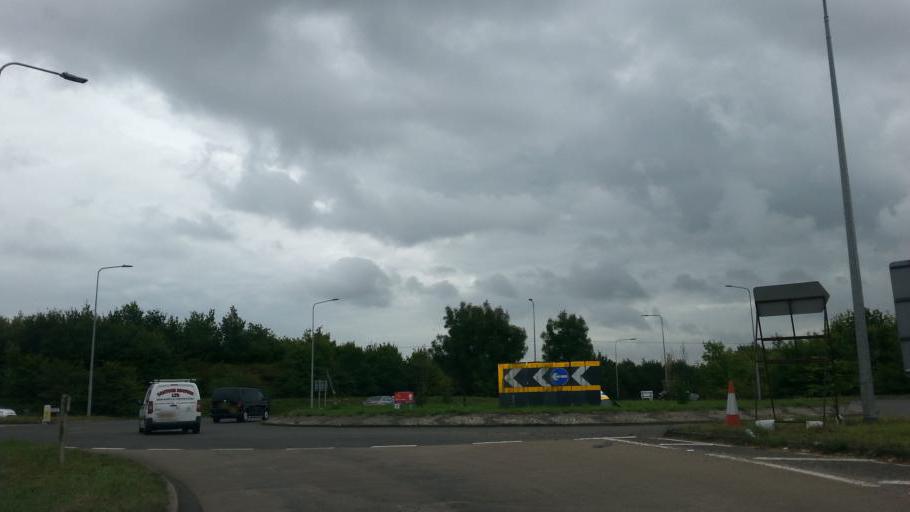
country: GB
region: England
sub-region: Essex
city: Chelmsford
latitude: 51.7874
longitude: 0.4873
